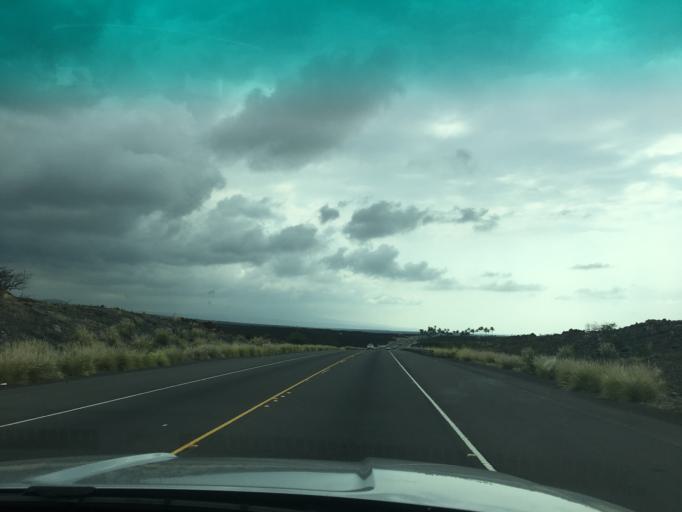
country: US
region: Hawaii
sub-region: Hawaii County
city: Waikoloa Village
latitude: 19.9405
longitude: -155.8379
